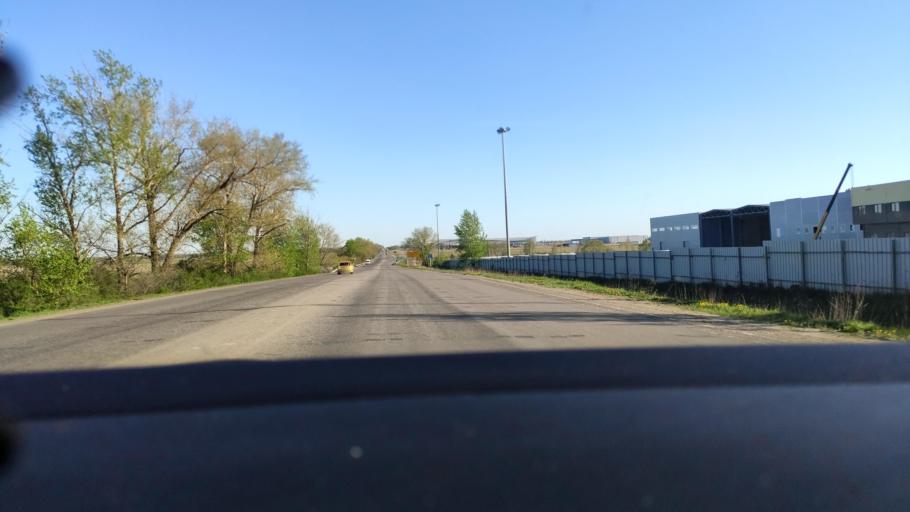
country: RU
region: Voronezj
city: Maslovka
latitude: 51.5547
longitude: 39.2793
